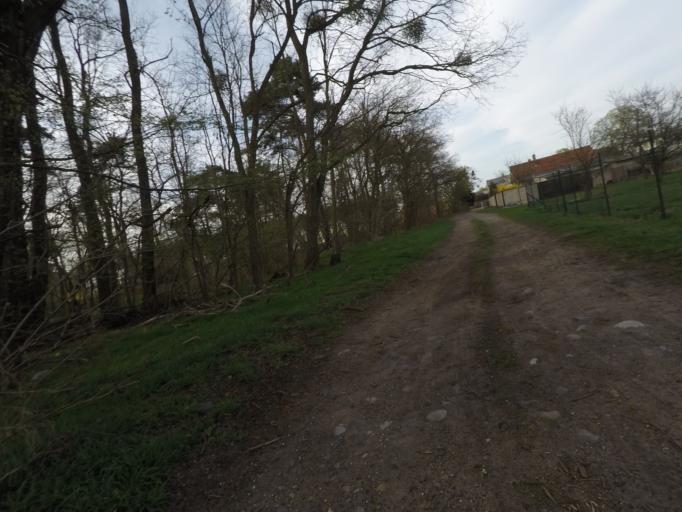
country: DE
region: Brandenburg
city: Marienwerder
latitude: 52.8505
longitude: 13.6708
